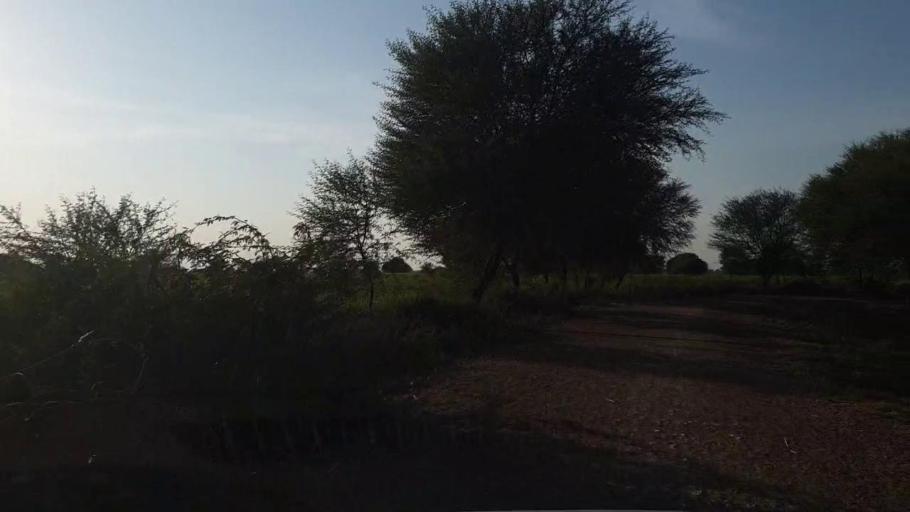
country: PK
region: Sindh
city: Chambar
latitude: 25.2839
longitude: 68.7992
